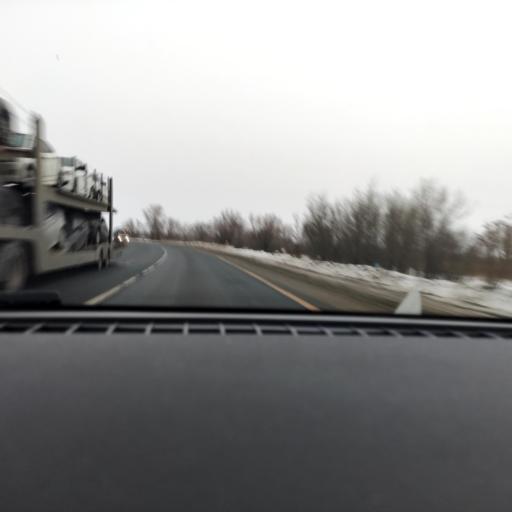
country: RU
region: Samara
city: Kinel'
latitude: 53.1508
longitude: 50.5124
